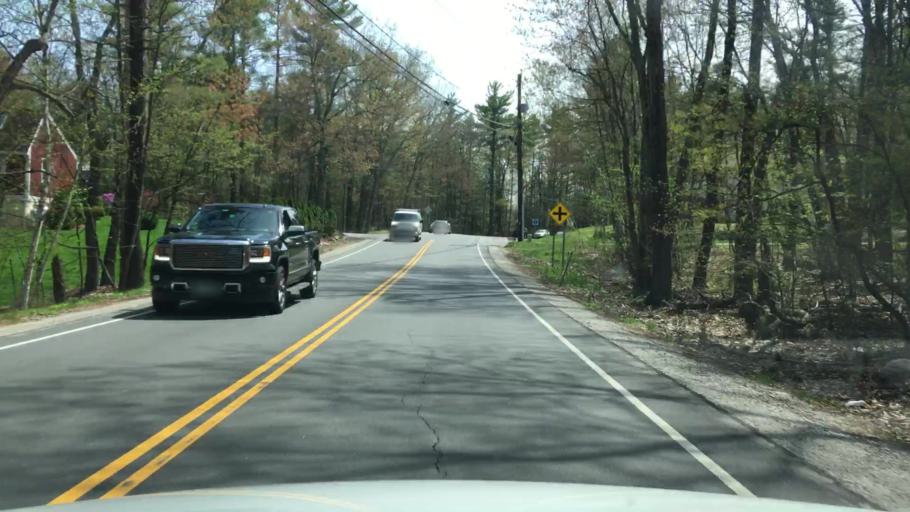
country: US
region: New Hampshire
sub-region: Rockingham County
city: Londonderry
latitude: 42.8374
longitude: -71.3621
